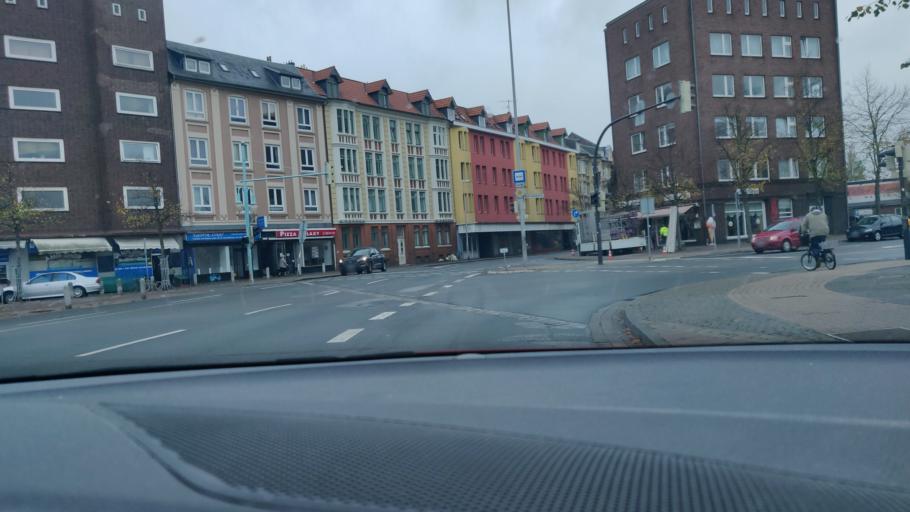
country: DE
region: Lower Saxony
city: Cuxhaven
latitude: 53.8650
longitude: 8.6965
